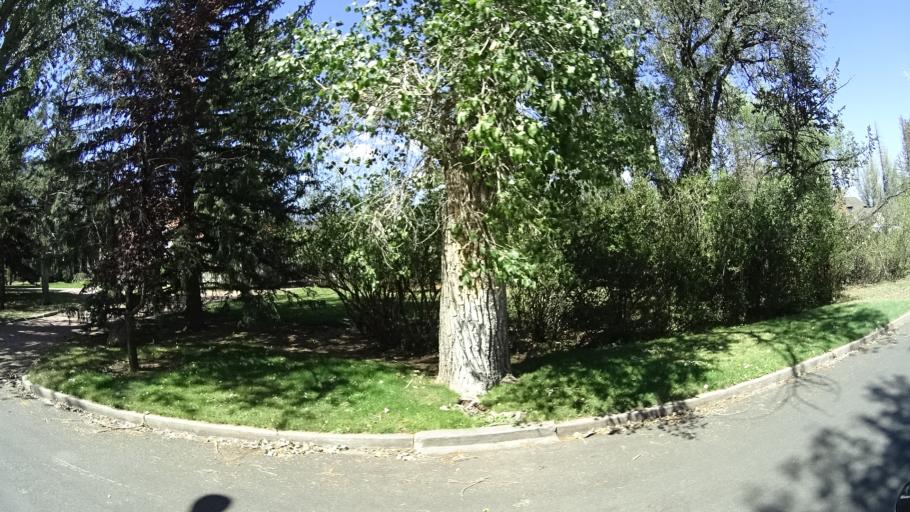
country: US
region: Colorado
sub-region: El Paso County
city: Colorado Springs
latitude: 38.7834
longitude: -104.8397
